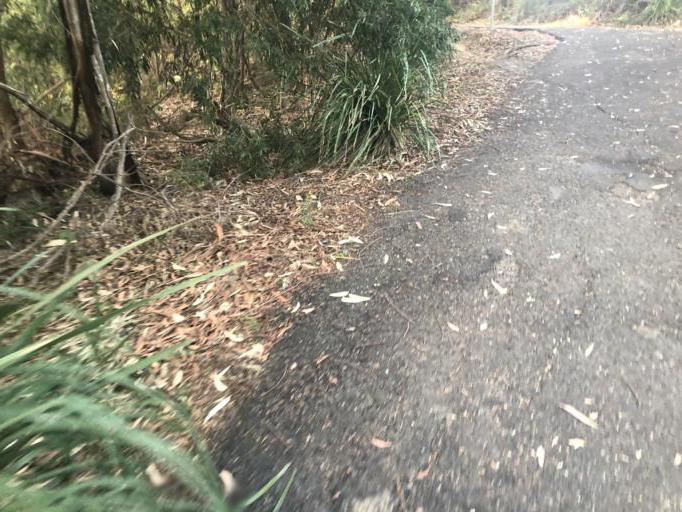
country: AU
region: New South Wales
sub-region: Coffs Harbour
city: Coffs Harbour
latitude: -30.3010
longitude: 153.1256
